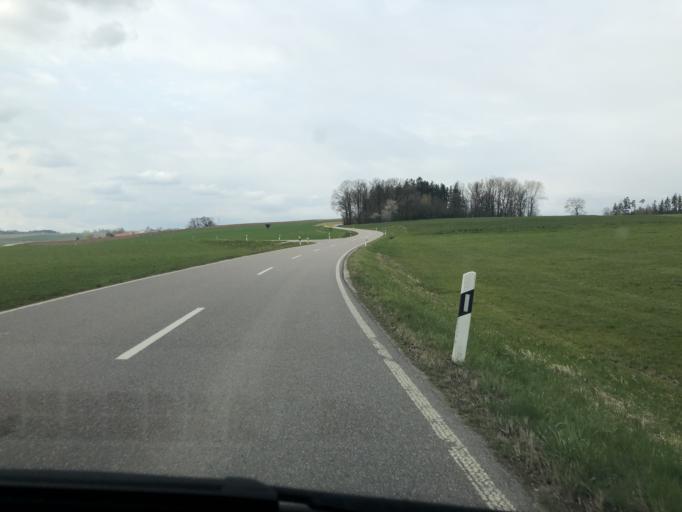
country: DE
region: Bavaria
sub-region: Upper Bavaria
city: Wolfersdorf
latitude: 48.4958
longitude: 11.6902
